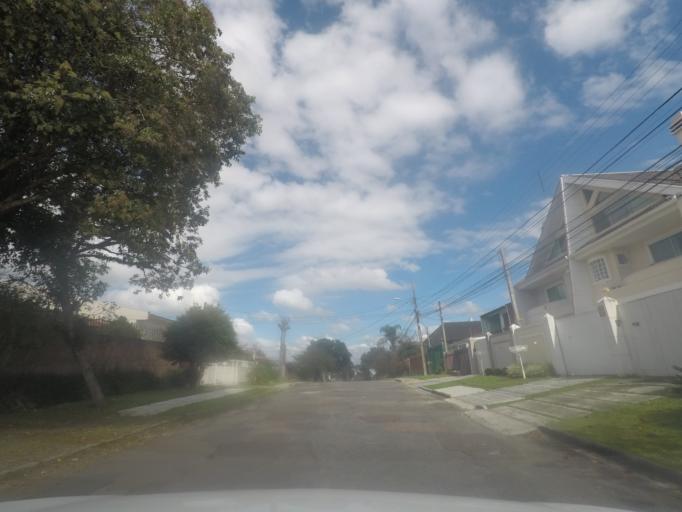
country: BR
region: Parana
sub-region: Pinhais
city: Pinhais
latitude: -25.4638
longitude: -49.2256
